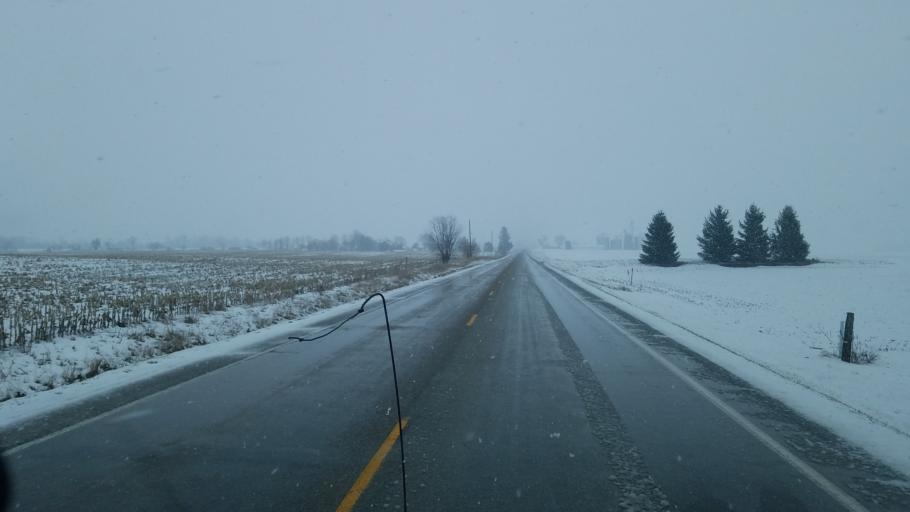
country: US
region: Indiana
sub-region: Wayne County
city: Hagerstown
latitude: 39.9755
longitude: -85.0778
